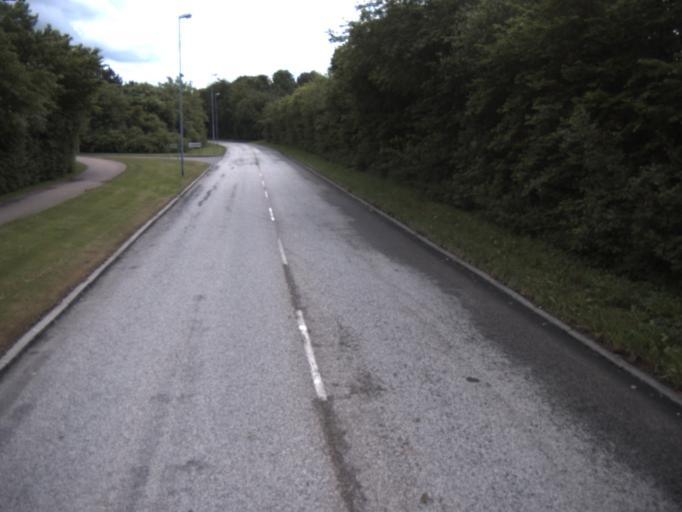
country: SE
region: Skane
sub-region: Helsingborg
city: Helsingborg
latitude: 56.0203
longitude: 12.7365
